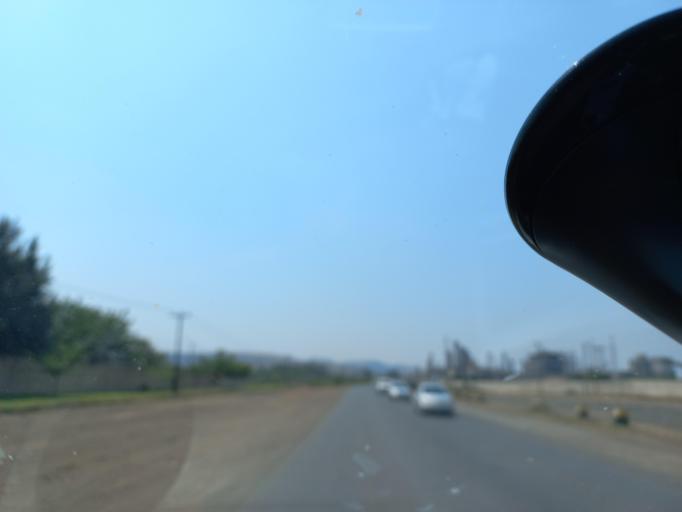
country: ZM
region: Lusaka
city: Kafue
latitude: -15.7520
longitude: 28.1645
